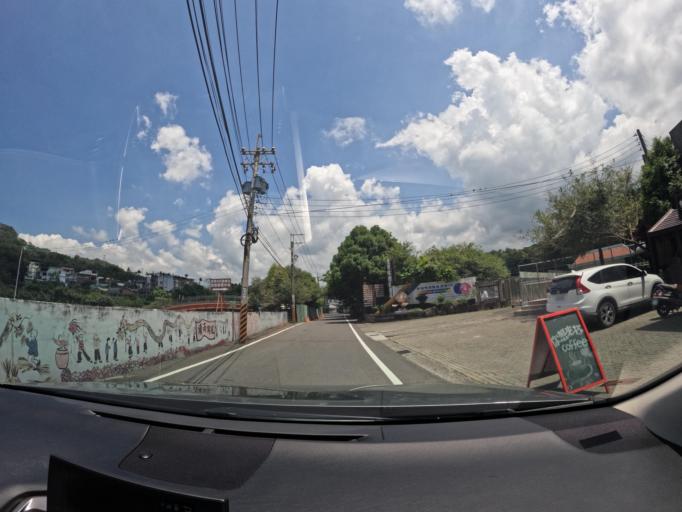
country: TW
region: Taiwan
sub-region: Miaoli
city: Miaoli
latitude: 24.4090
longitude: 120.7827
